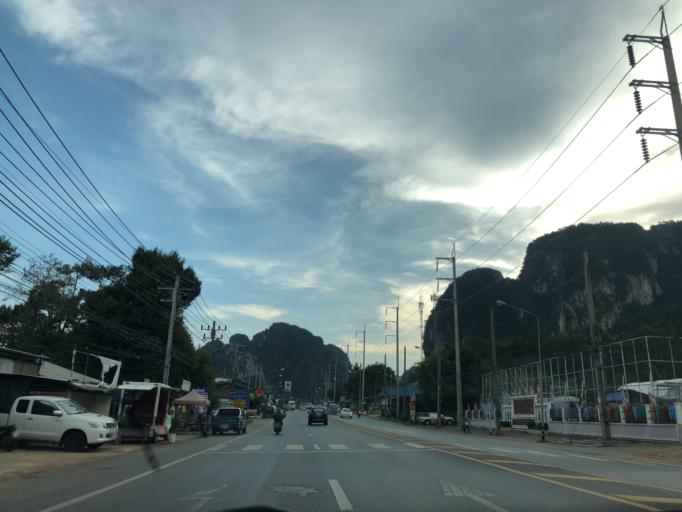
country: TH
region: Krabi
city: Krabi
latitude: 8.0817
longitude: 98.8597
